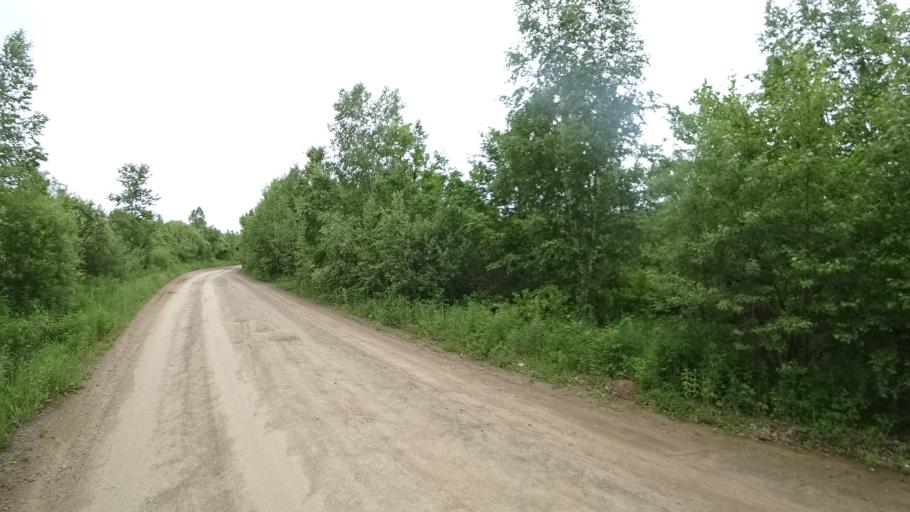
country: RU
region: Primorskiy
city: Arsen'yev
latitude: 44.1932
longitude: 133.3102
